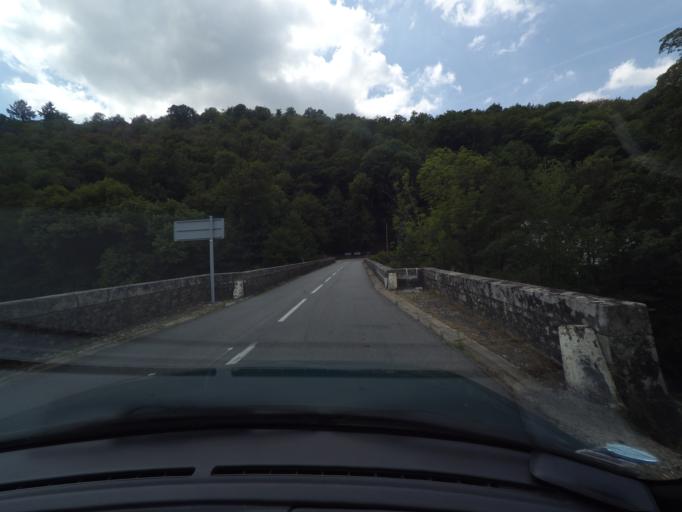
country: FR
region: Limousin
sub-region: Departement de la Haute-Vienne
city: Bosmie-l'Aiguille
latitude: 45.7695
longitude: 1.2238
